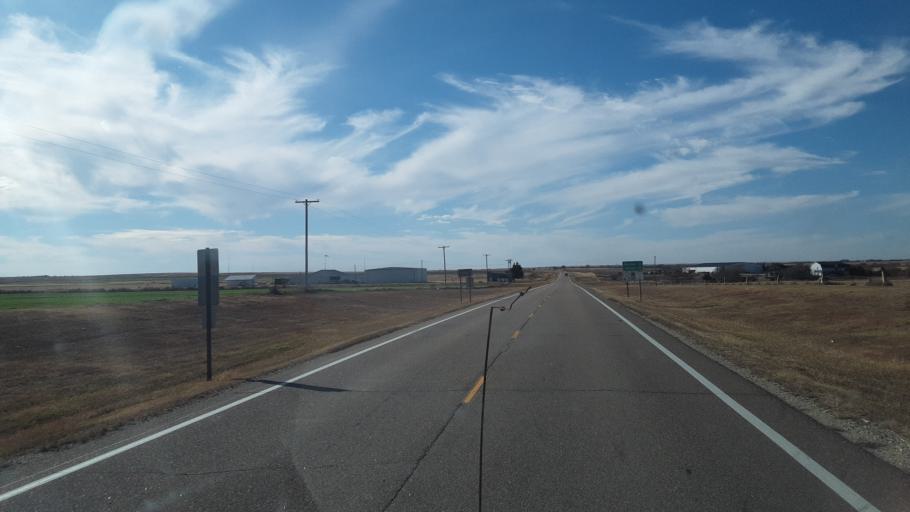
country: US
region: Kansas
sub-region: Edwards County
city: Kinsley
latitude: 38.1897
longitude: -99.5302
